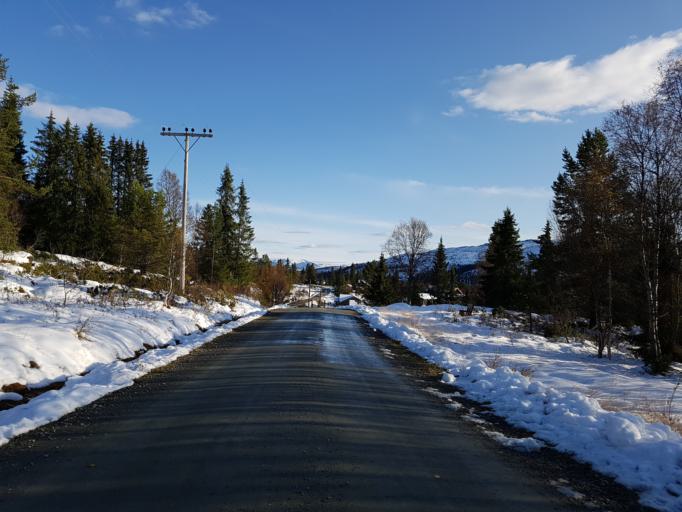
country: NO
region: Oppland
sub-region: Sel
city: Otta
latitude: 61.8151
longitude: 9.6800
